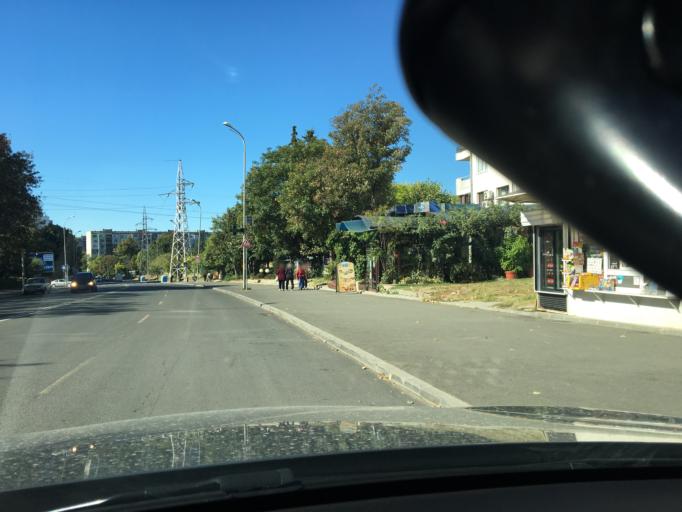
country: BG
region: Burgas
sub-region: Obshtina Burgas
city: Burgas
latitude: 42.5201
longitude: 27.4517
